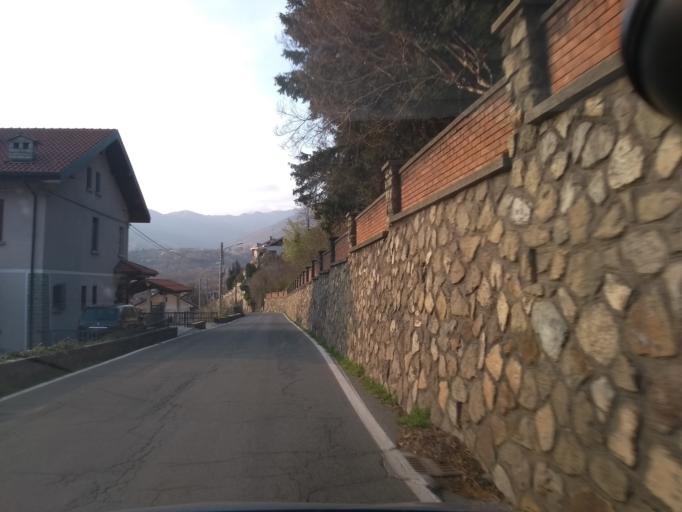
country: IT
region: Piedmont
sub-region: Provincia di Torino
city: Lanzo Torinese
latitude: 45.2776
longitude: 7.4830
